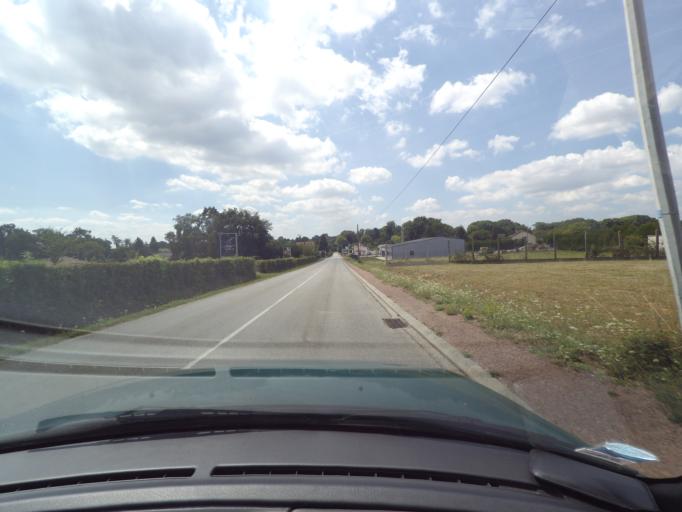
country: FR
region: Limousin
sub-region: Departement de la Haute-Vienne
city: Isle
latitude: 45.7858
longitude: 1.2349
